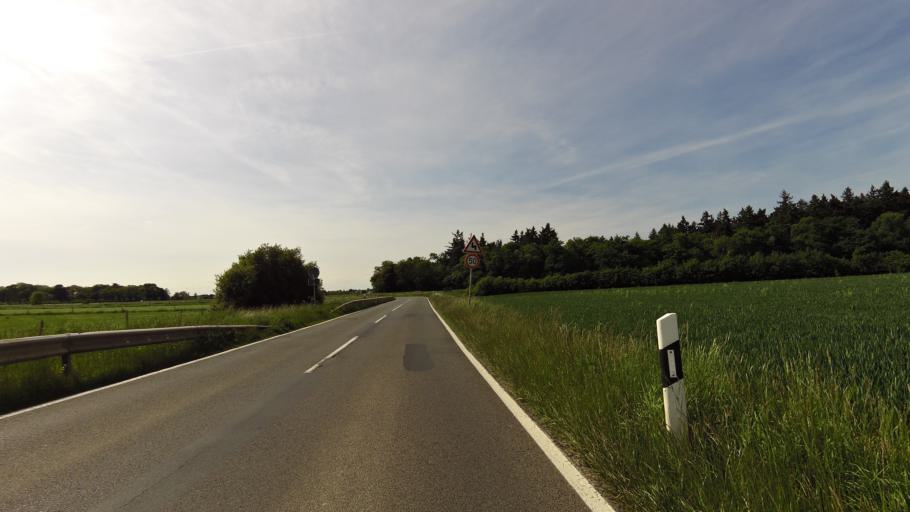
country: DE
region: North Rhine-Westphalia
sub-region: Regierungsbezirk Koln
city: Rheinbach
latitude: 50.6644
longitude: 6.9697
